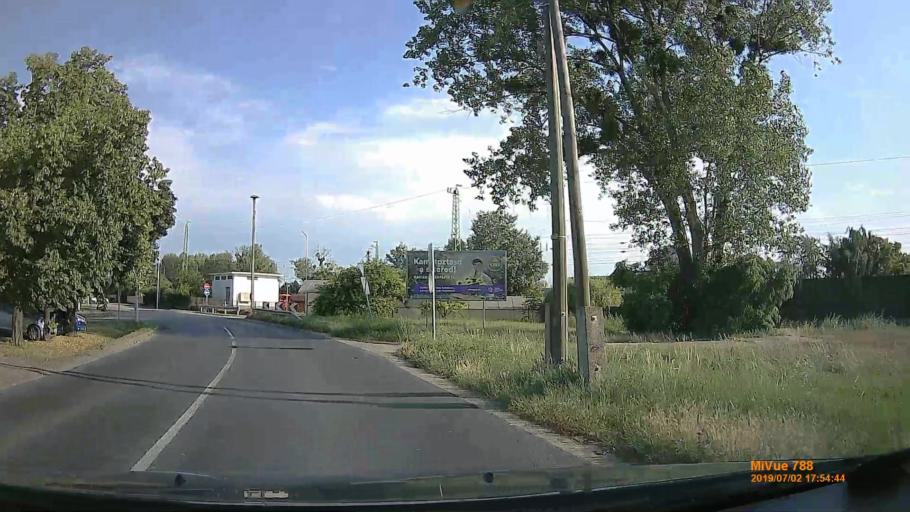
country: HU
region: Gyor-Moson-Sopron
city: Mosonmagyarovar
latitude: 47.8521
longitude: 17.2647
